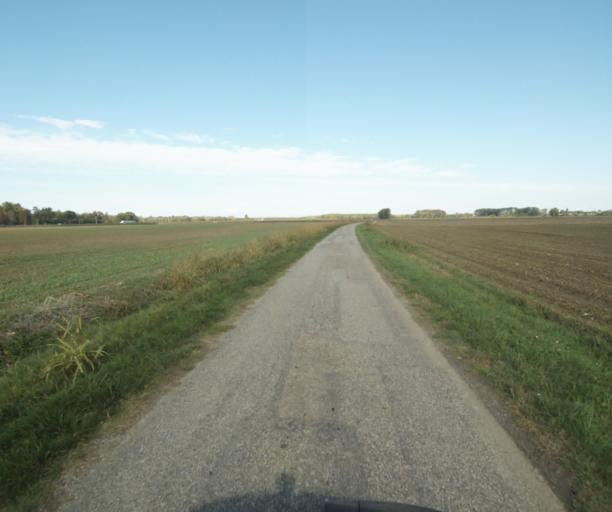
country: FR
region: Midi-Pyrenees
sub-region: Departement du Tarn-et-Garonne
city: Finhan
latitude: 43.8866
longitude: 1.2210
